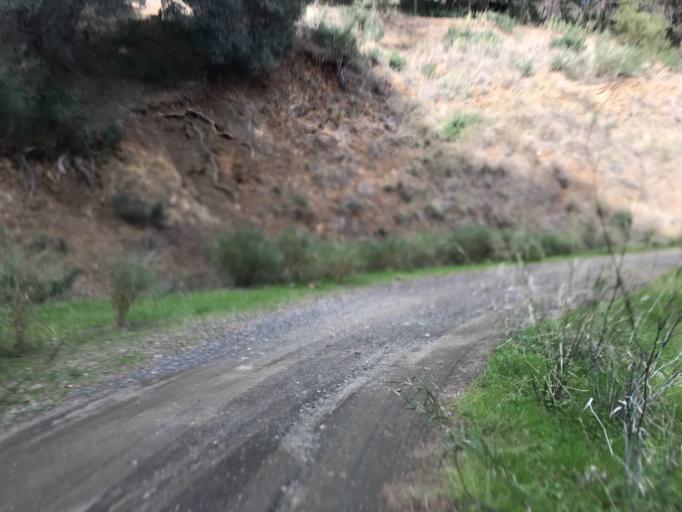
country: ES
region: Andalusia
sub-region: Provincia de Malaga
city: Malaga
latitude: 36.8028
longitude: -4.4058
